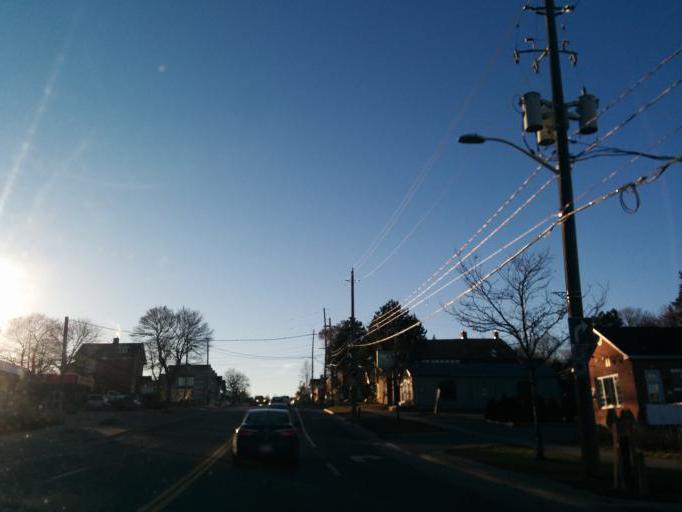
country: CA
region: Ontario
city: Orangeville
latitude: 43.9207
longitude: -80.0908
